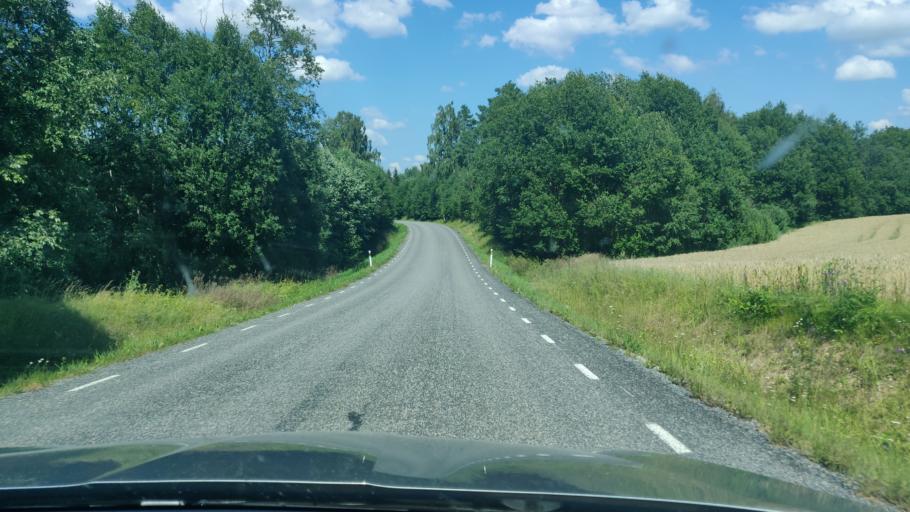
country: EE
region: Tartu
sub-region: Elva linn
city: Elva
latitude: 58.1500
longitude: 26.4735
